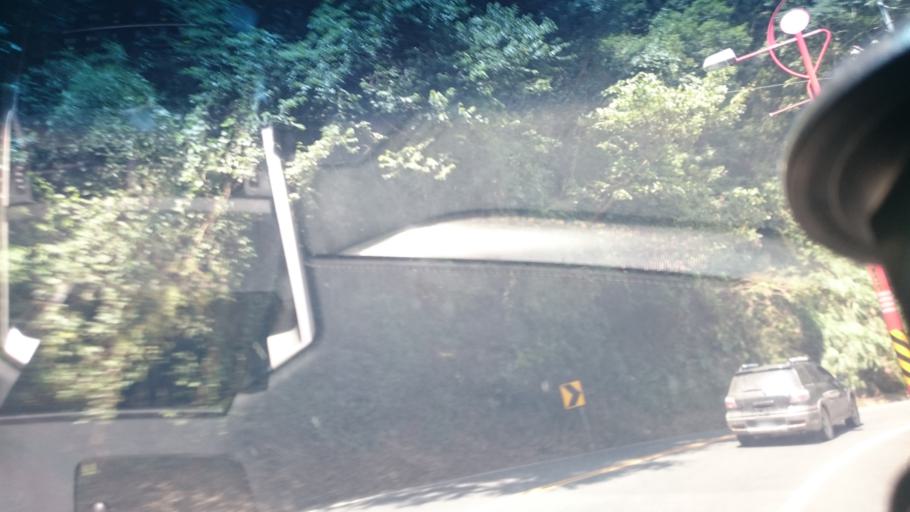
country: TW
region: Taiwan
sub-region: Nantou
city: Puli
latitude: 24.0273
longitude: 121.1428
